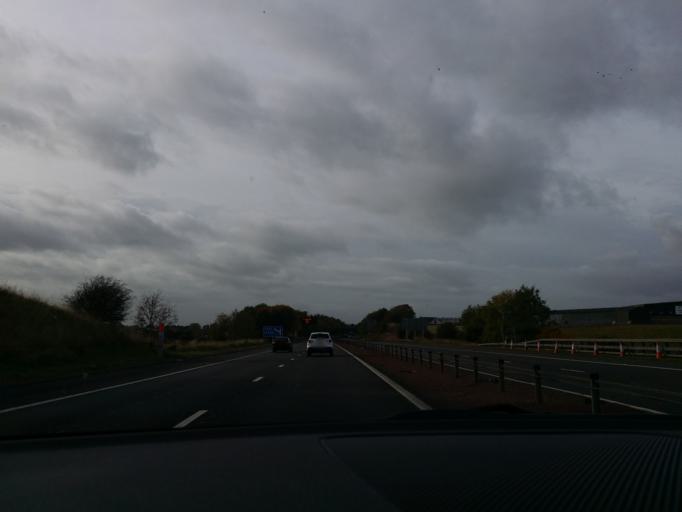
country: GB
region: Scotland
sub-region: Fife
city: Limekilns
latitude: 55.9831
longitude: -3.5268
